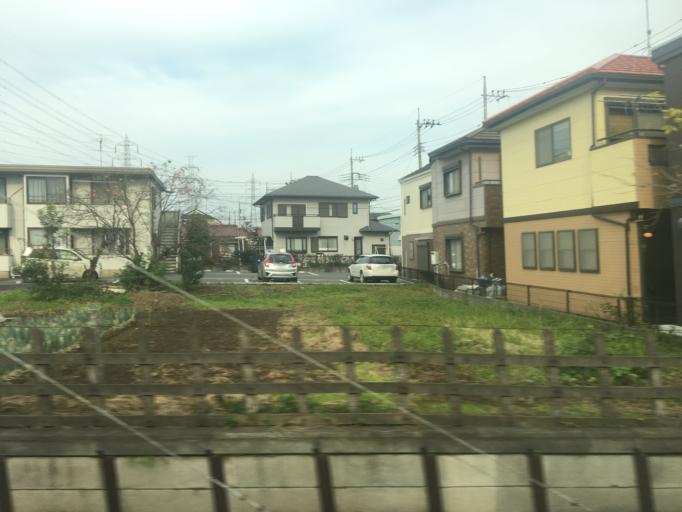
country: JP
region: Saitama
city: Sayama
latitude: 35.8694
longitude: 139.4273
